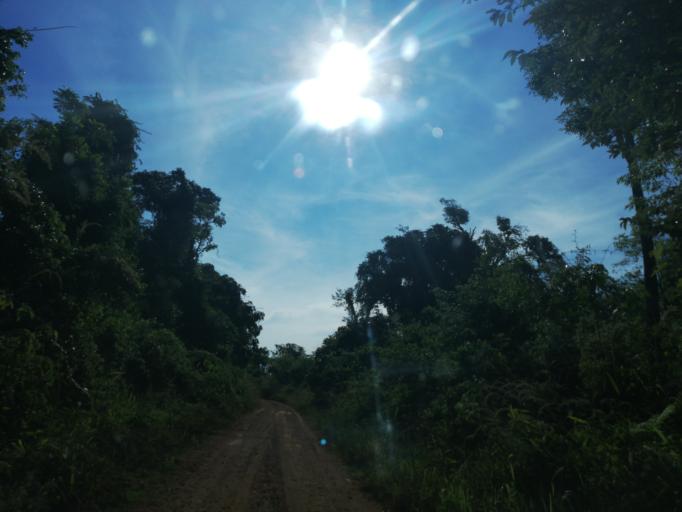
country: AR
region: Misiones
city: Dos de Mayo
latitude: -27.0144
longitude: -54.4301
